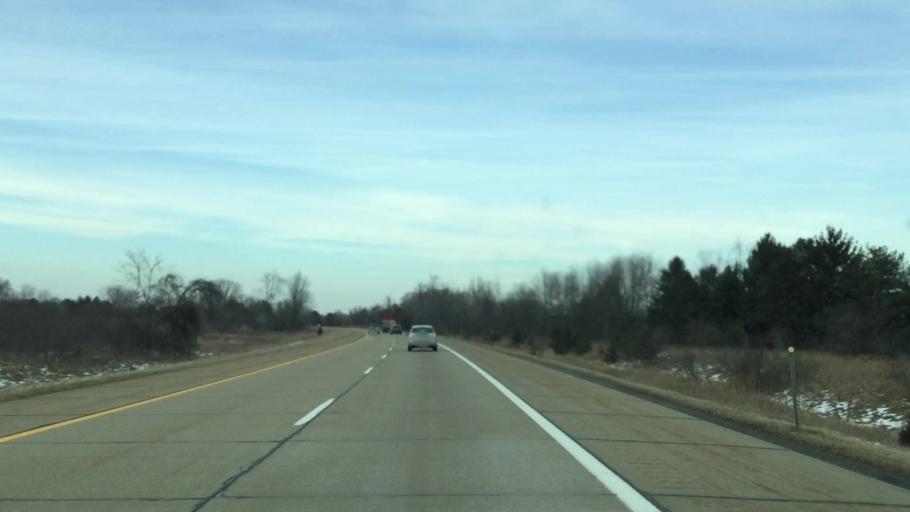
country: US
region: Michigan
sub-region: Eaton County
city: Olivet
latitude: 42.3801
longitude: -84.9689
